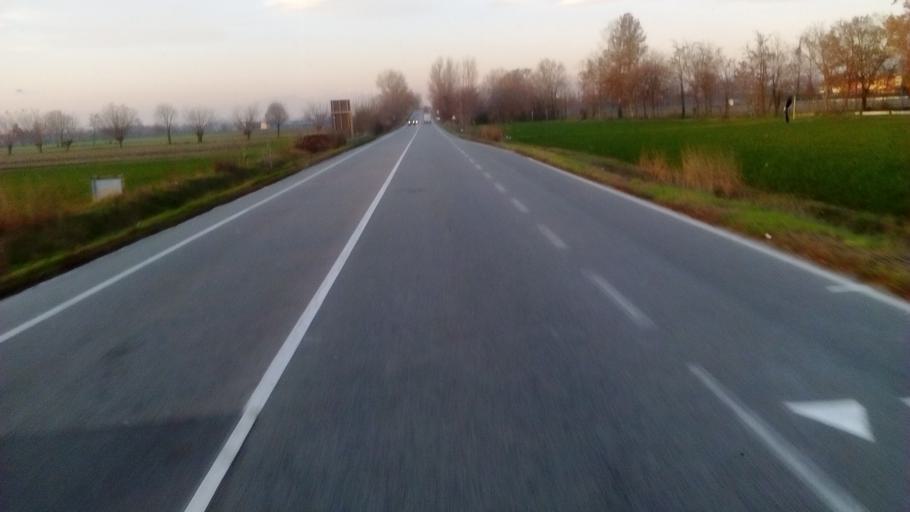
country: IT
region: Lombardy
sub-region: Provincia di Cremona
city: Soncino
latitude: 45.4010
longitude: 9.8567
